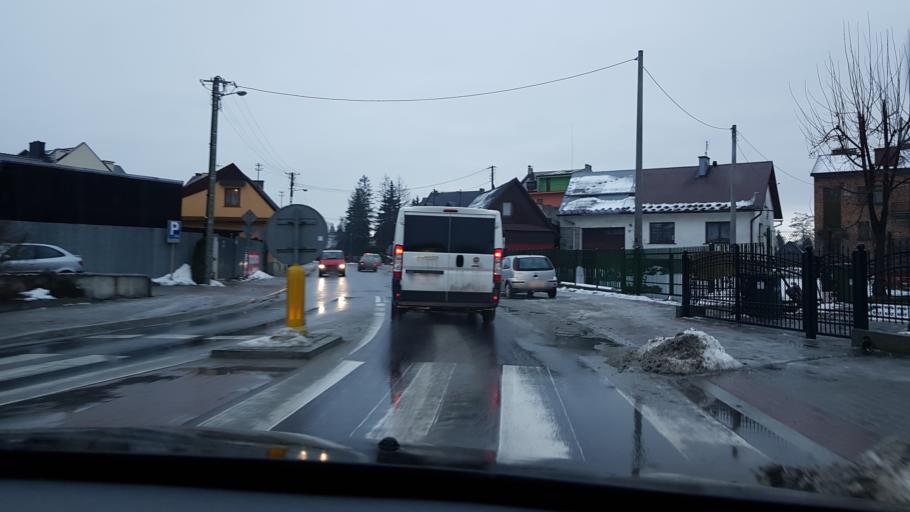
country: PL
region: Lesser Poland Voivodeship
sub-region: Powiat nowotarski
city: Nowy Targ
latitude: 49.4805
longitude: 20.0428
